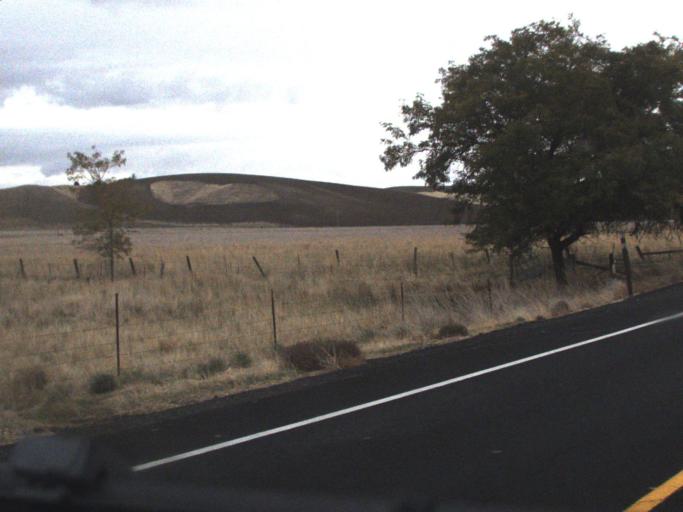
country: US
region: Washington
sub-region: Whitman County
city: Colfax
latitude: 46.8112
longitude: -117.6201
